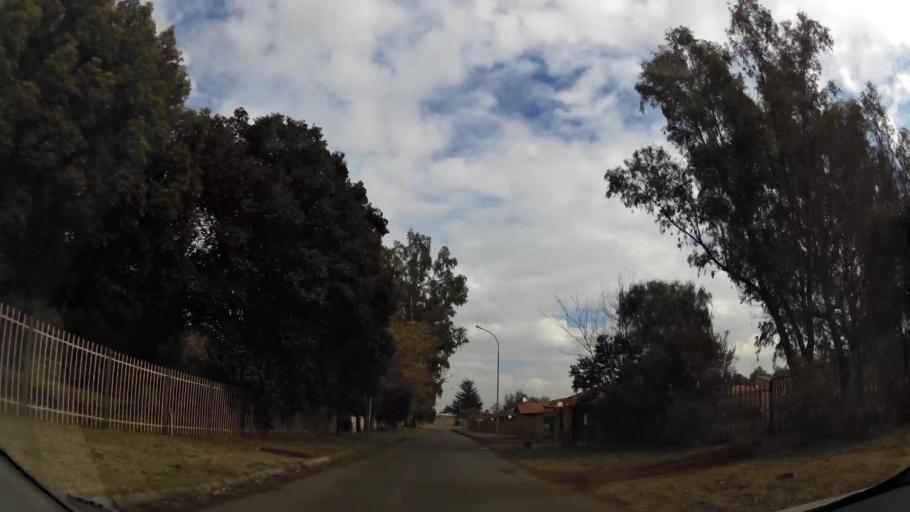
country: ZA
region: Gauteng
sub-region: Sedibeng District Municipality
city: Meyerton
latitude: -26.5878
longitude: 28.0102
